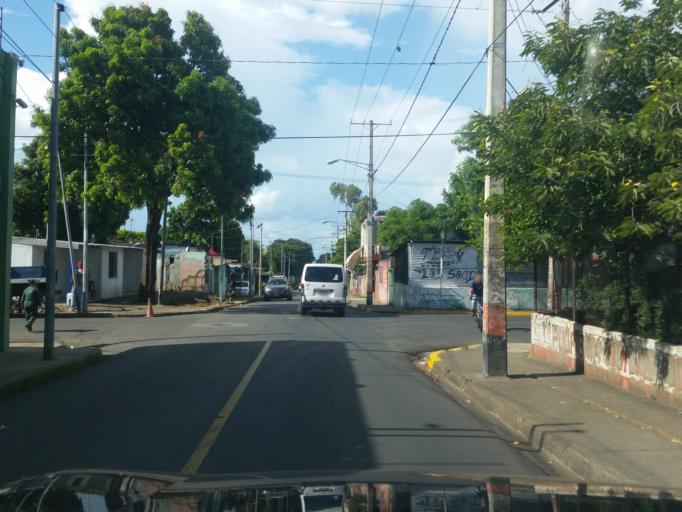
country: NI
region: Managua
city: Managua
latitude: 12.1460
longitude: -86.2684
